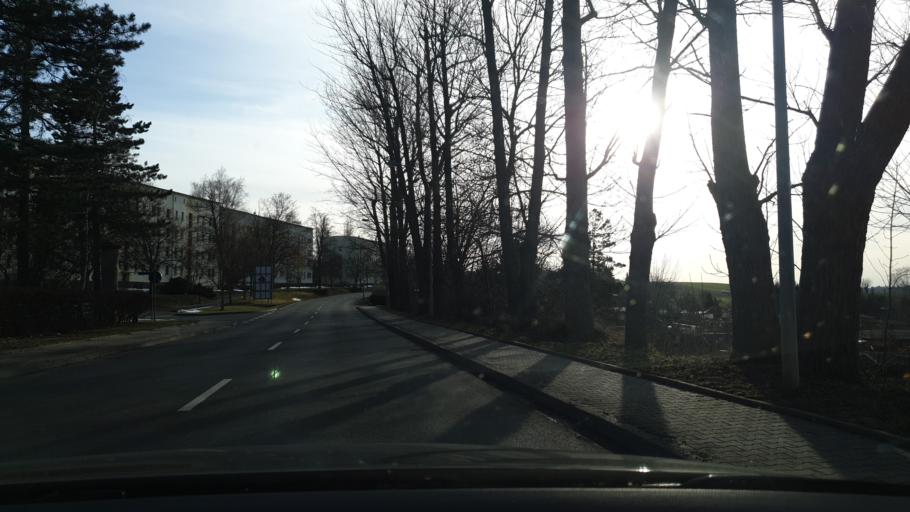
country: DE
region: Thuringia
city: Zeulenroda
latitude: 50.6463
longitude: 11.9726
